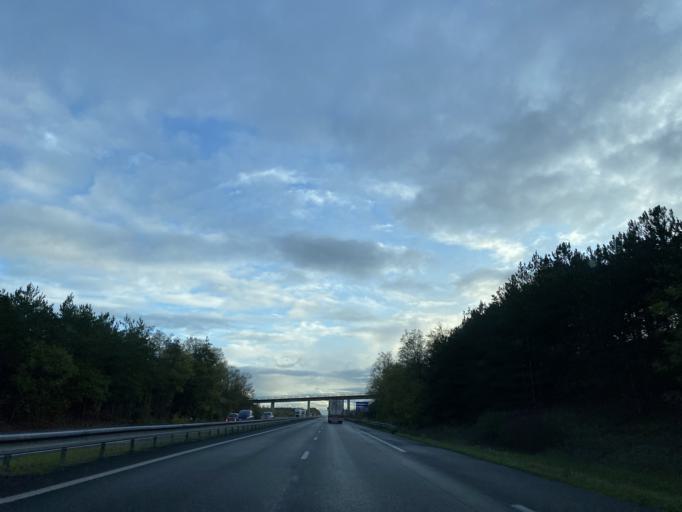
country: FR
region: Centre
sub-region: Departement du Cher
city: Foecy
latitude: 47.1562
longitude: 2.1834
